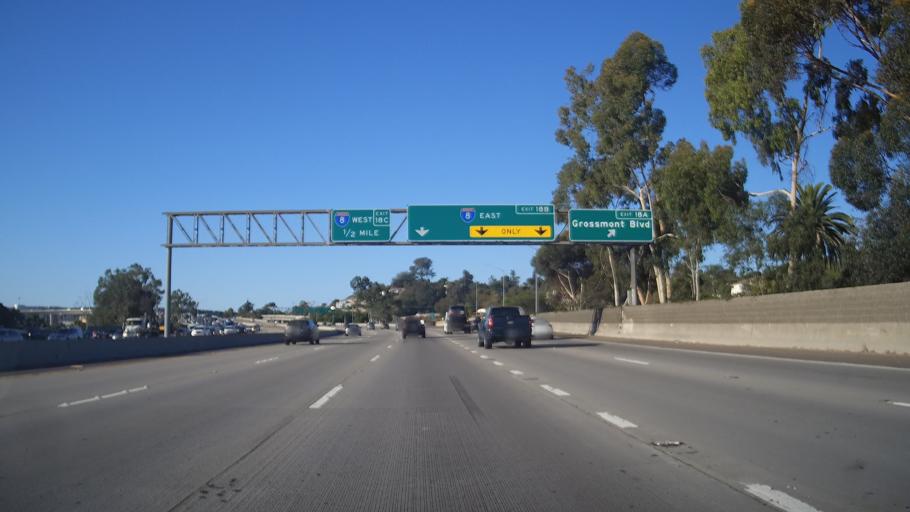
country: US
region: California
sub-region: San Diego County
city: La Mesa
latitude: 32.7695
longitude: -117.0018
